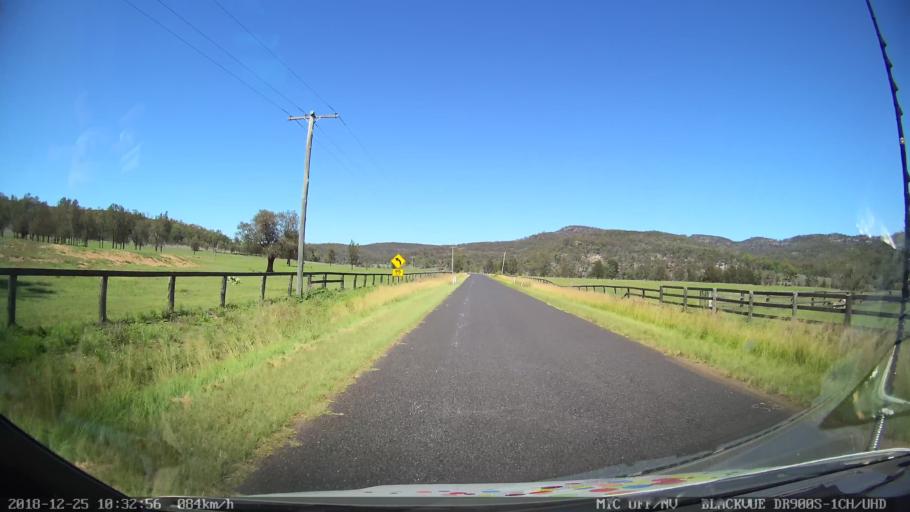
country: AU
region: New South Wales
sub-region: Upper Hunter Shire
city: Merriwa
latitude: -32.3785
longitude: 150.4121
